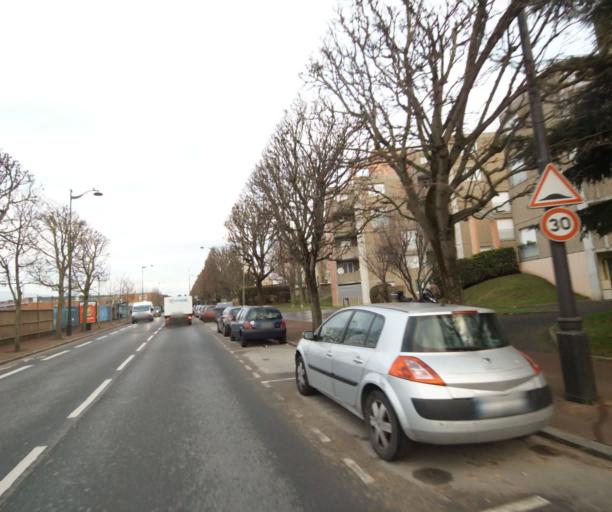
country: FR
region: Ile-de-France
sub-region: Departement des Hauts-de-Seine
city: Rueil-Malmaison
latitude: 48.8727
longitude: 2.2024
